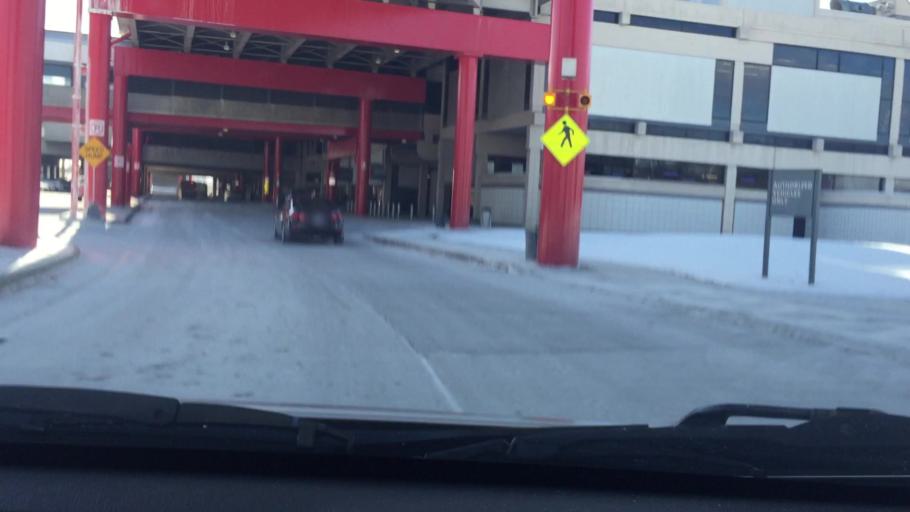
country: US
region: Pennsylvania
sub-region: Allegheny County
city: Carnot-Moon
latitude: 40.4973
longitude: -80.2556
